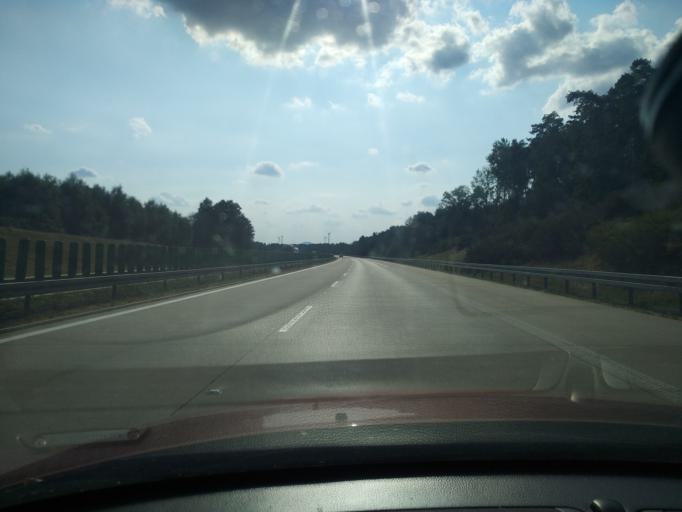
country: PL
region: Lower Silesian Voivodeship
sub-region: Powiat lubanski
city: Siekierczyn
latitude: 51.1997
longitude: 15.1332
